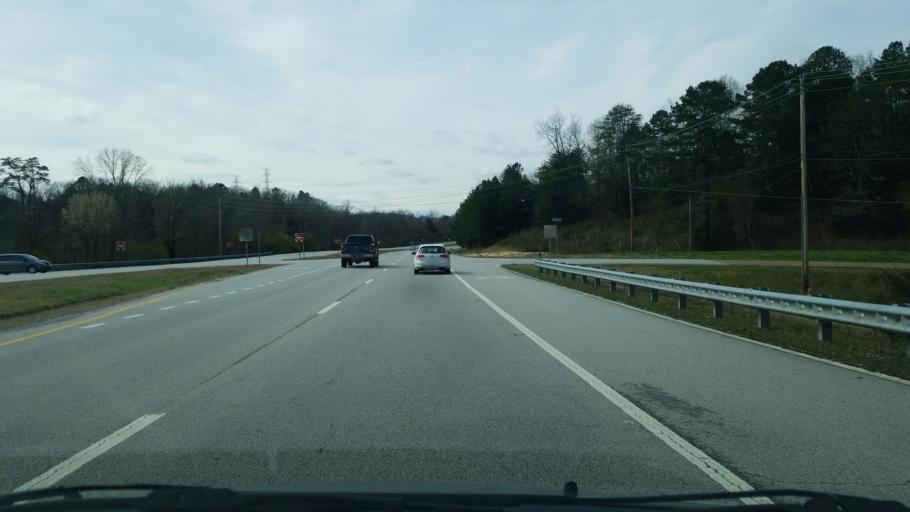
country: US
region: Tennessee
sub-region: Hamilton County
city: Lakesite
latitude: 35.1687
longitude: -85.0778
